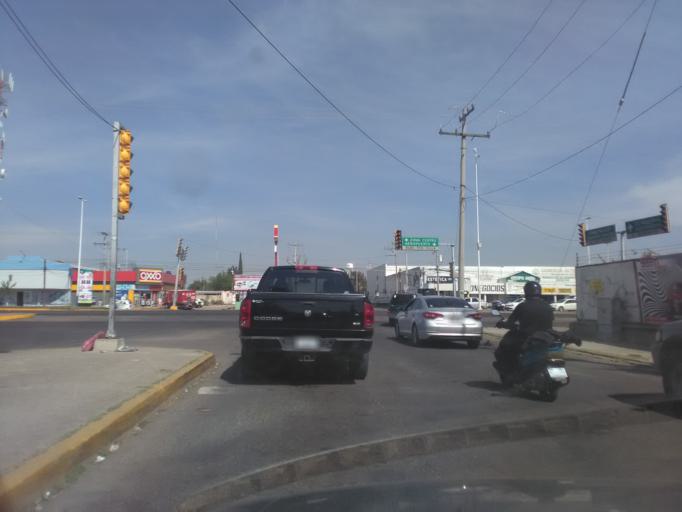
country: MX
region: Durango
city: Victoria de Durango
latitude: 24.0574
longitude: -104.6114
